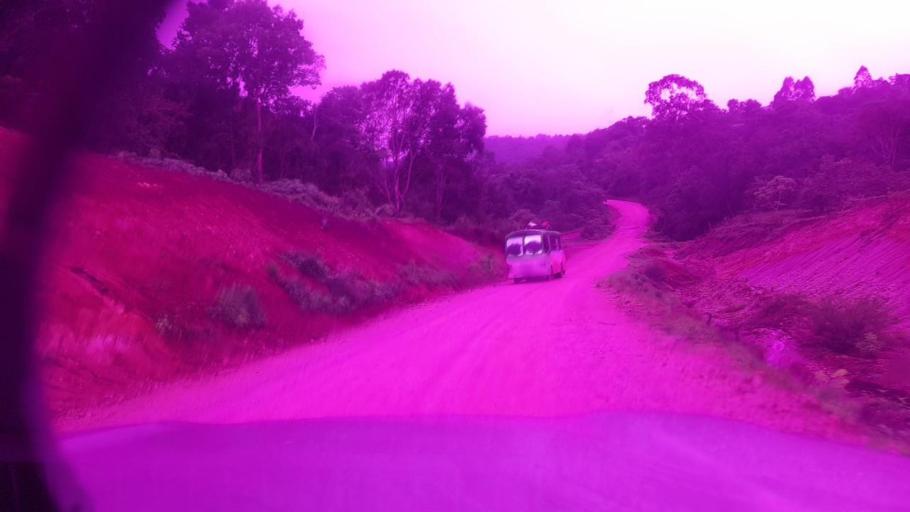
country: ET
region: Southern Nations, Nationalities, and People's Region
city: Bonga
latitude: 7.4494
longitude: 36.1350
